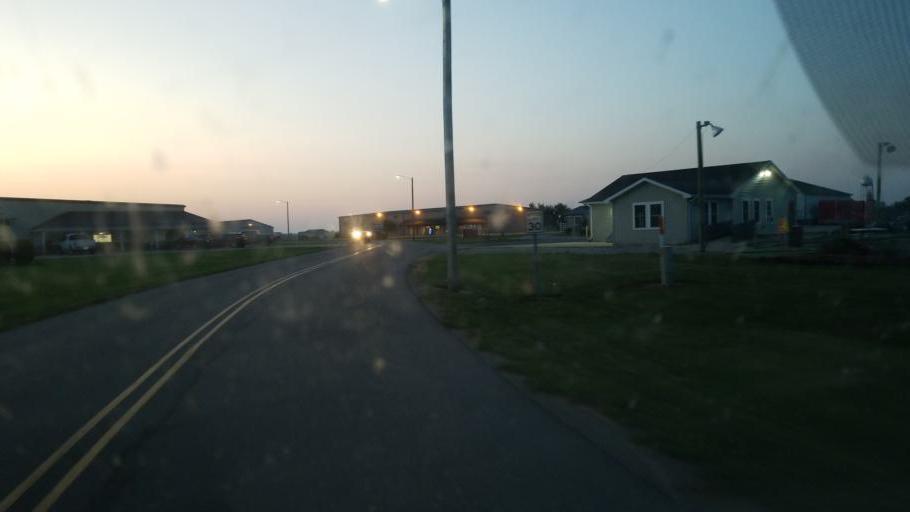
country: US
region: Indiana
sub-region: Elkhart County
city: Middlebury
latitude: 41.6852
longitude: -85.5798
